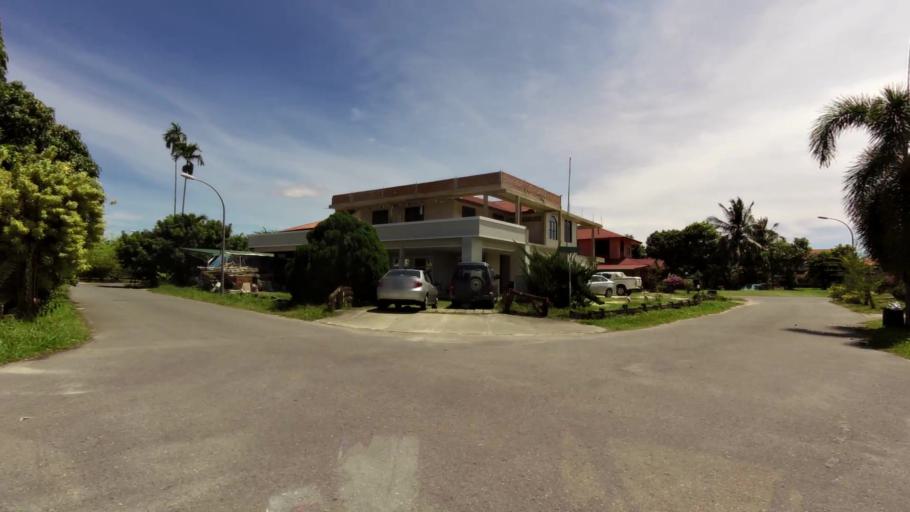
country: BN
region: Belait
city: Kuala Belait
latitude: 4.5880
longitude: 114.2235
